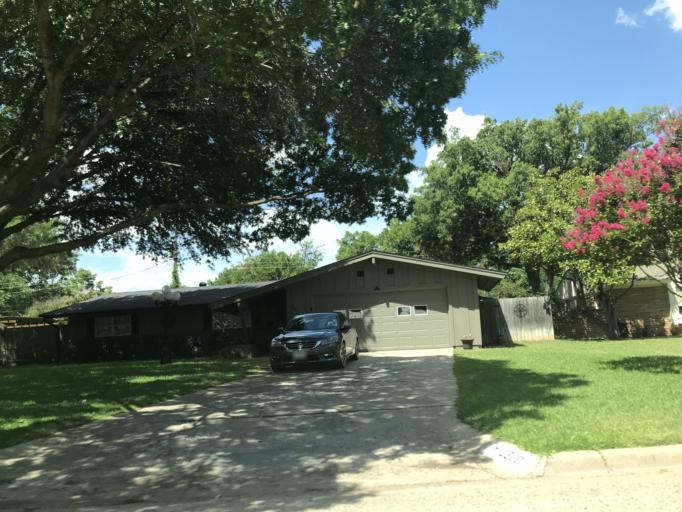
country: US
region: Texas
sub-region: Taylor County
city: Abilene
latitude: 32.4226
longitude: -99.7678
